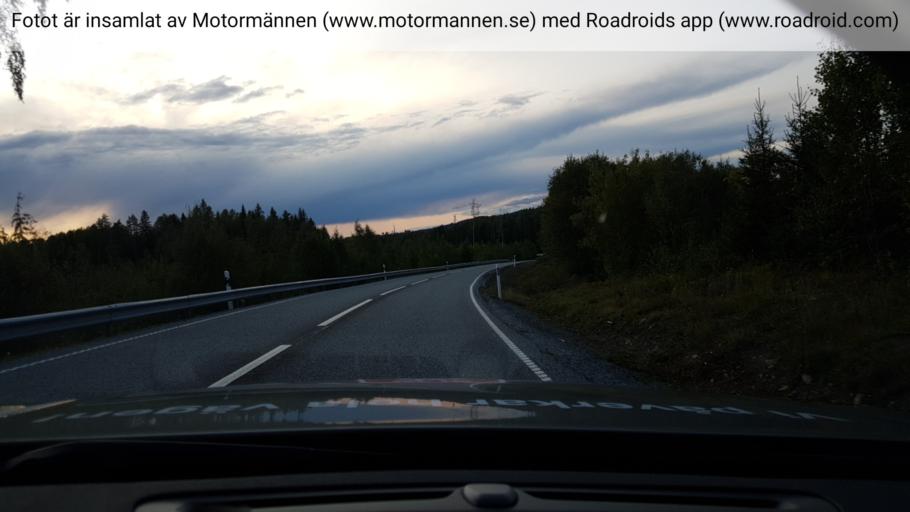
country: SE
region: OErebro
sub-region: Hallefors Kommun
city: Haellefors
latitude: 59.8135
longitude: 14.6633
